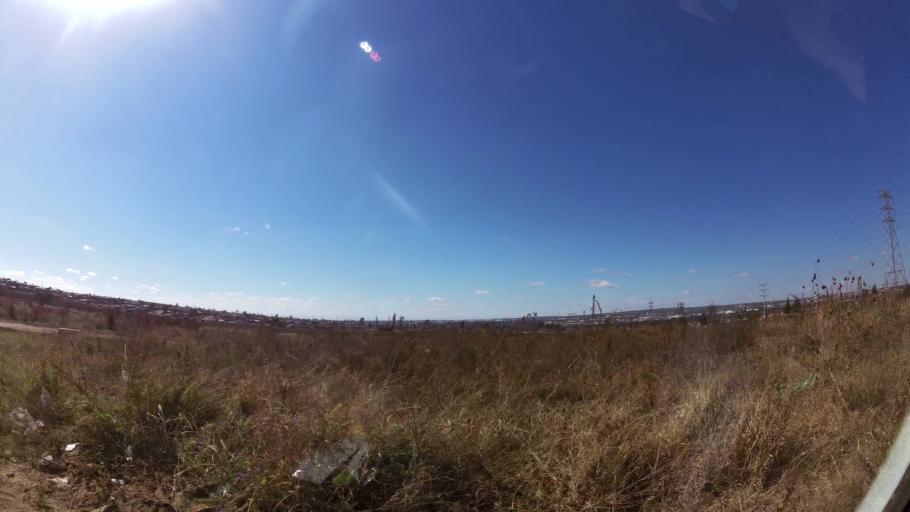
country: ZA
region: Limpopo
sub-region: Capricorn District Municipality
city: Polokwane
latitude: -23.8889
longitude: 29.4123
